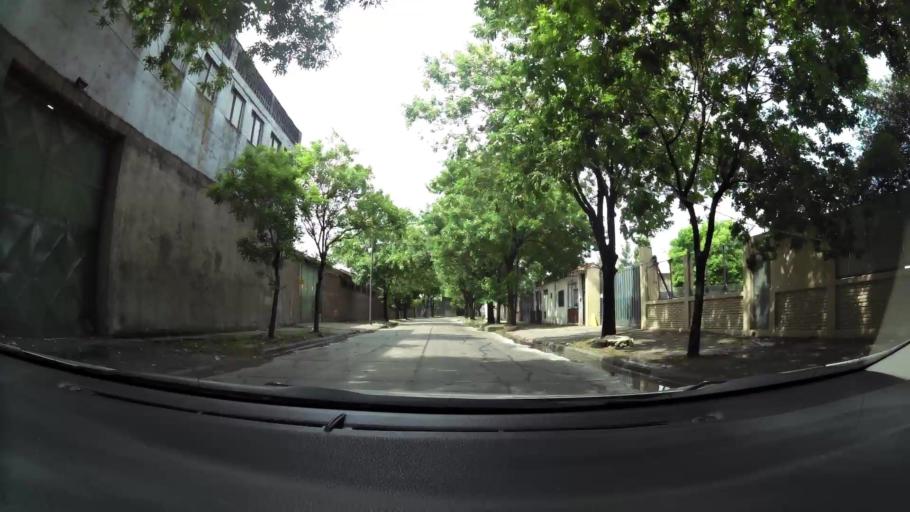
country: AR
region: Buenos Aires
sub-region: Partido de Lanus
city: Lanus
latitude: -34.6583
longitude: -58.4214
